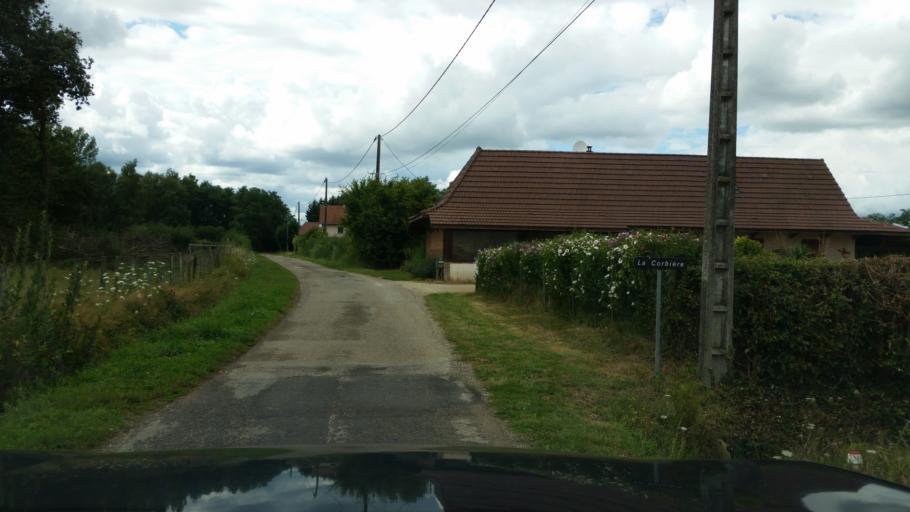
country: FR
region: Bourgogne
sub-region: Departement de Saone-et-Loire
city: Saint-Germain-du-Bois
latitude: 46.7400
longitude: 5.2795
